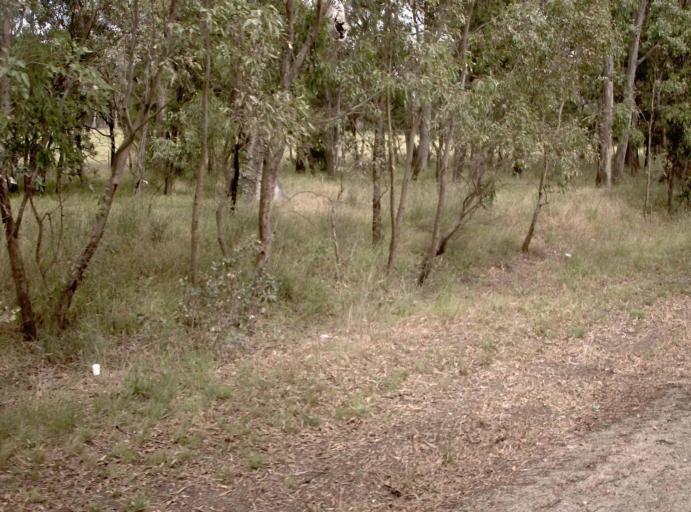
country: AU
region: Victoria
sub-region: Wellington
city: Sale
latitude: -37.8887
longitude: 147.0660
